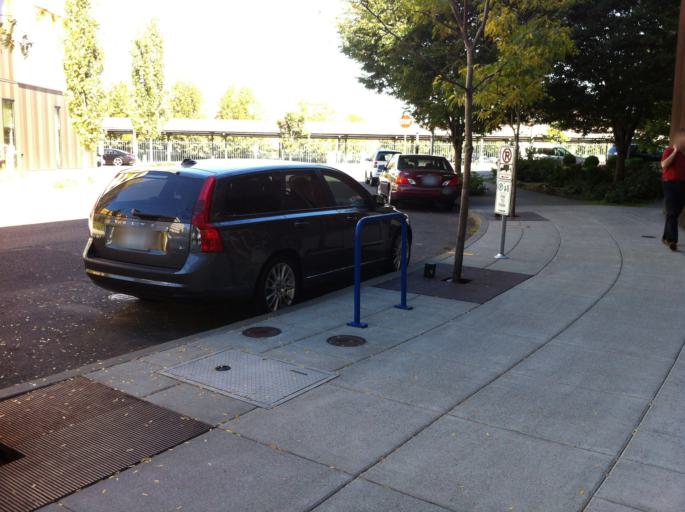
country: US
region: Oregon
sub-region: Multnomah County
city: Portland
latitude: 45.5311
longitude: -122.6795
